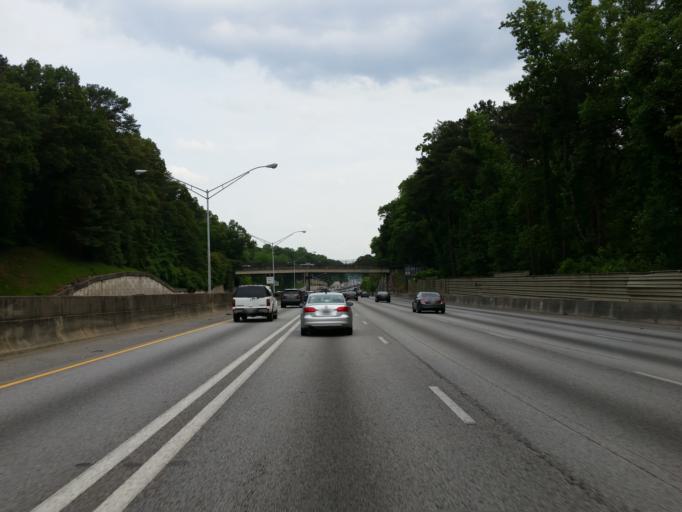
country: US
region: Georgia
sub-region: Cobb County
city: Vinings
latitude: 33.8281
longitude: -84.4251
